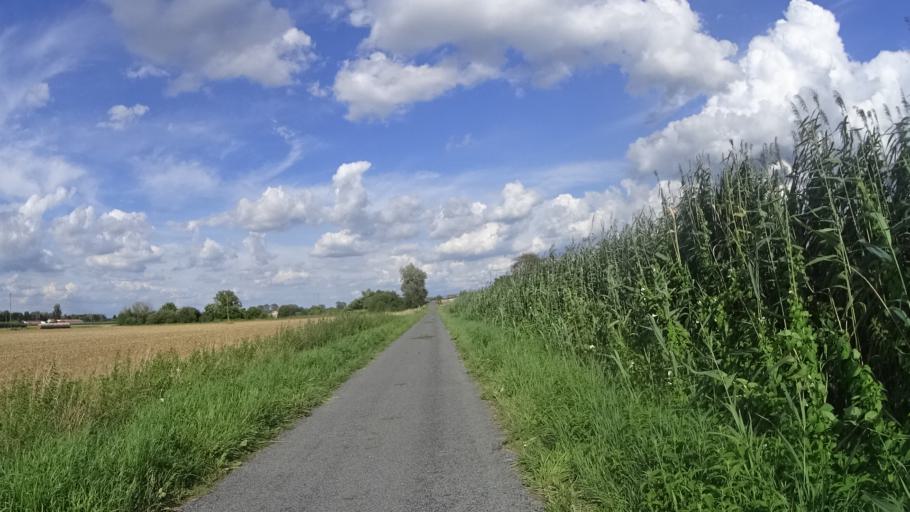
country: FR
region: Champagne-Ardenne
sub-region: Departement de la Marne
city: Sermaize-les-Bains
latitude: 48.7866
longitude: 4.8828
